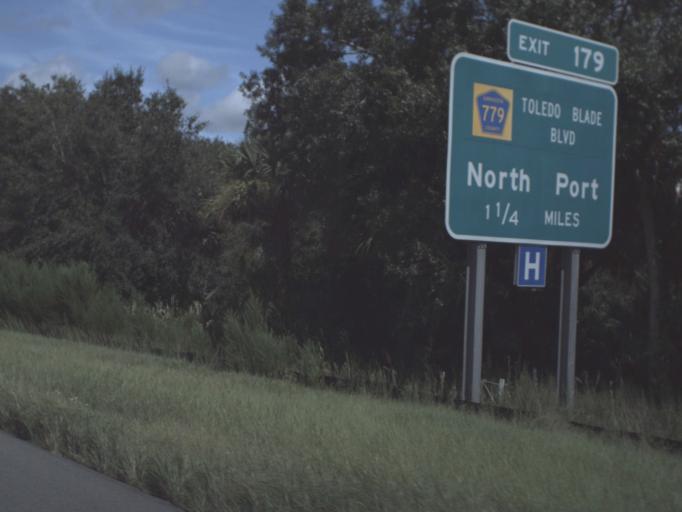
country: US
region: Florida
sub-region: Sarasota County
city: North Port
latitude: 27.0972
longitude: -82.1277
